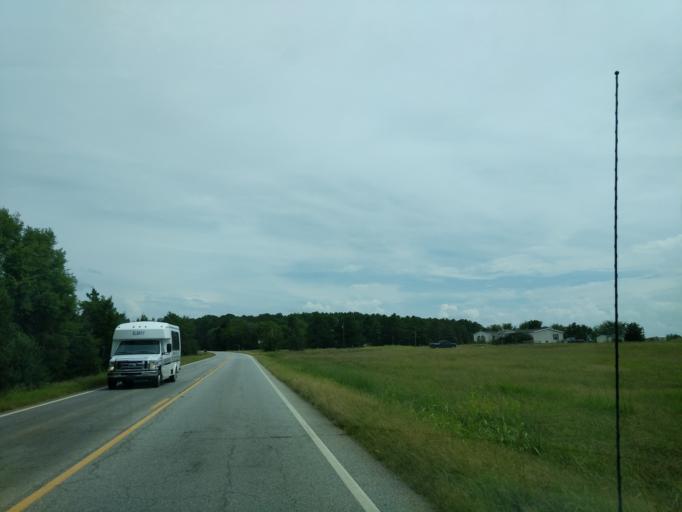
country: US
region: Georgia
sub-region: Elbert County
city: Elberton
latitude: 34.0726
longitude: -82.7443
